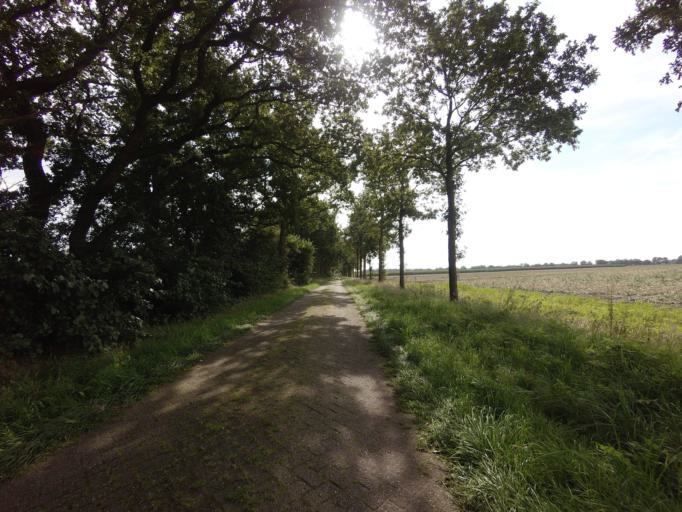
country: NL
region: Drenthe
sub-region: Gemeente Coevorden
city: Sleen
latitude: 52.7842
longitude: 6.7263
